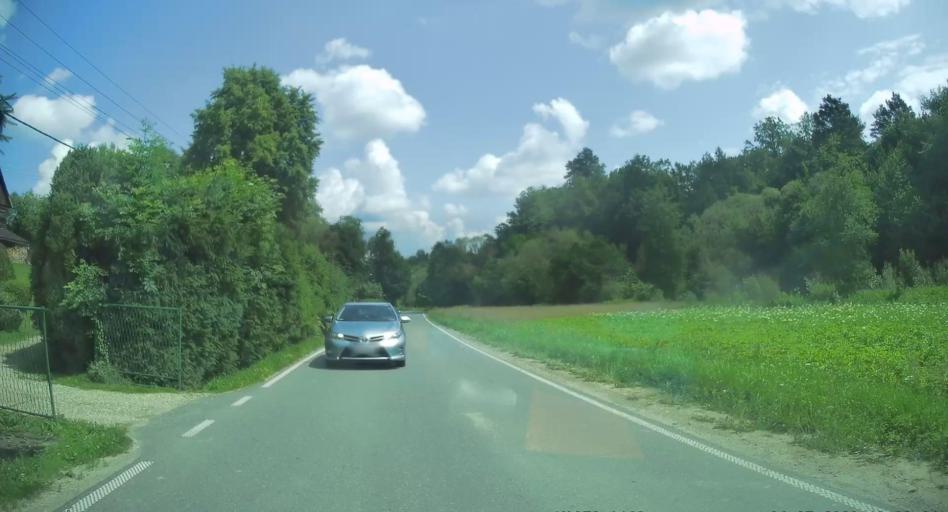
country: PL
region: Lesser Poland Voivodeship
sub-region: Powiat nowosadecki
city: Korzenna
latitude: 49.7460
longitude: 20.7698
